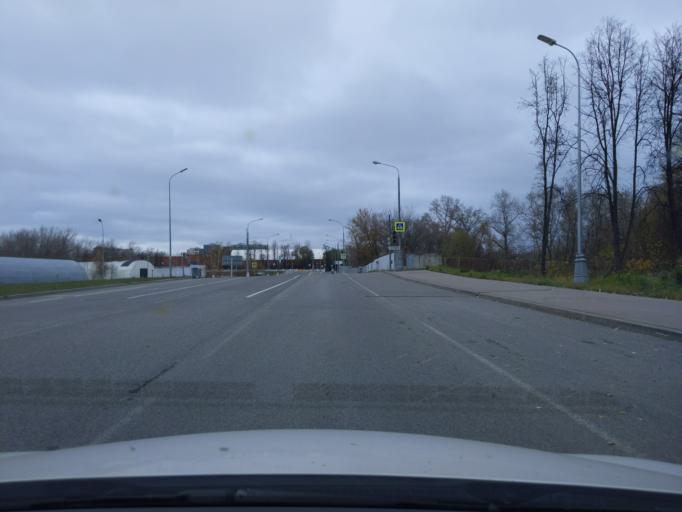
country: RU
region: Moscow
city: Pokrovskoye-Streshnevo
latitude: 55.8188
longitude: 37.4442
